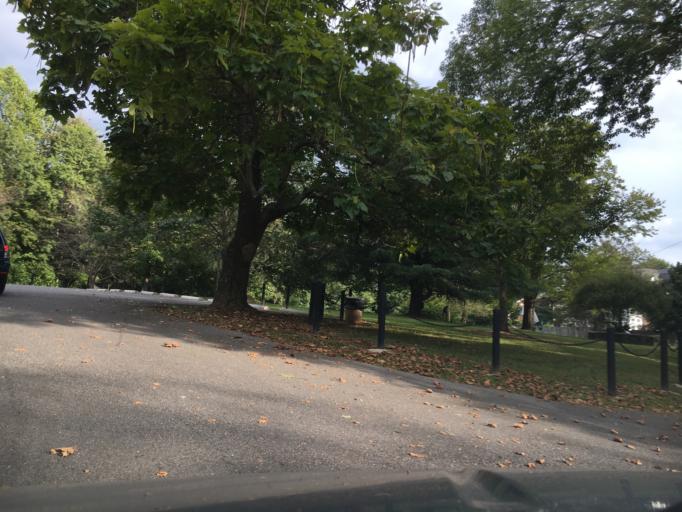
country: US
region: Virginia
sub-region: City of Lynchburg
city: Lynchburg
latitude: 37.4375
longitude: -79.1632
